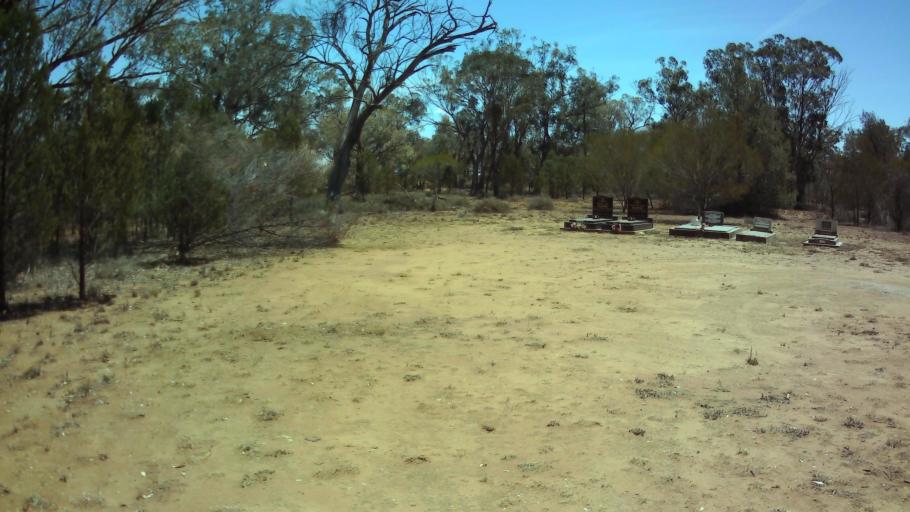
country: AU
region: New South Wales
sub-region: Weddin
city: Grenfell
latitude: -33.8433
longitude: 147.7242
